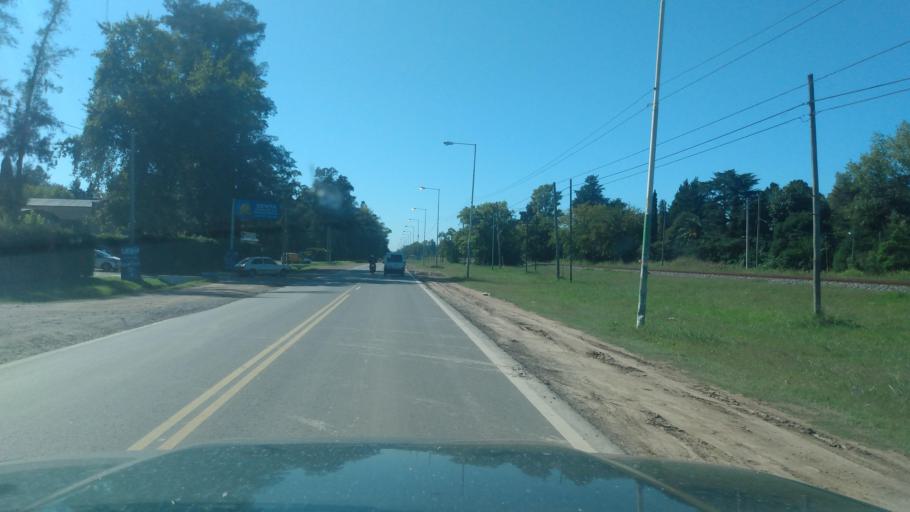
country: AR
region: Buenos Aires
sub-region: Partido de General Rodriguez
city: General Rodriguez
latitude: -34.6020
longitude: -58.9813
